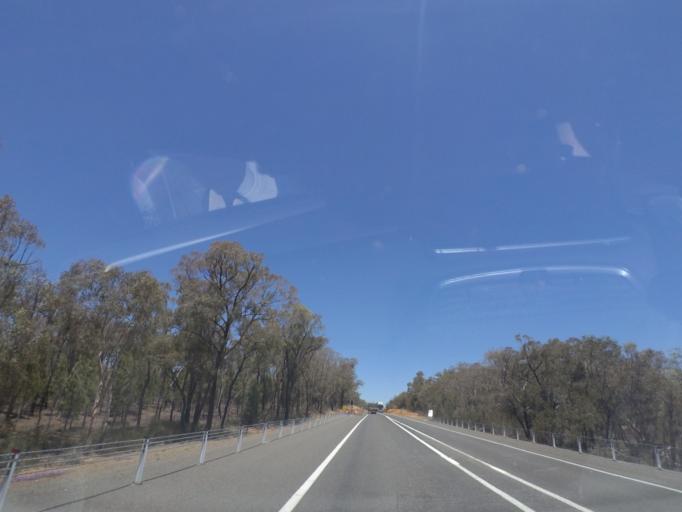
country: AU
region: New South Wales
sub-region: Warrumbungle Shire
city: Coonabarabran
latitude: -30.9212
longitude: 149.4326
